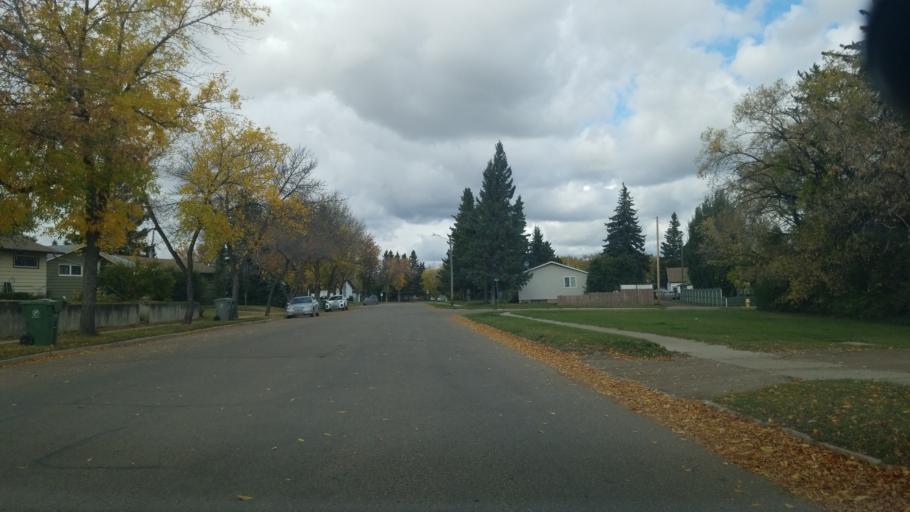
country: CA
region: Saskatchewan
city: Lloydminster
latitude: 53.2792
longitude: -110.0198
